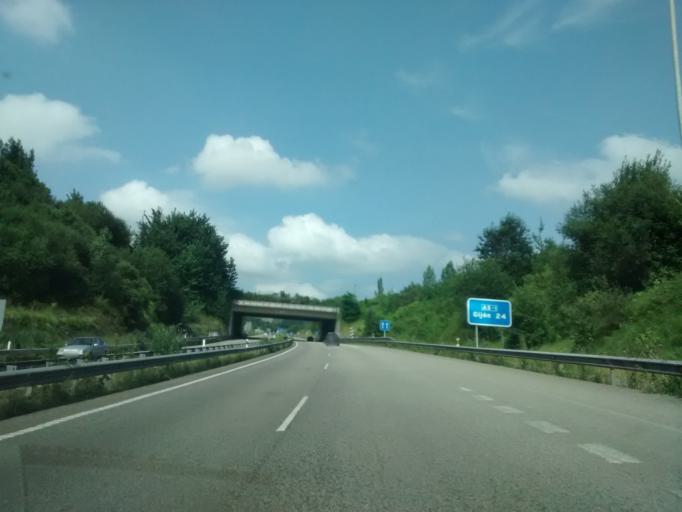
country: ES
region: Asturias
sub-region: Province of Asturias
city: Sama
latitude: 43.3307
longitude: -5.7220
